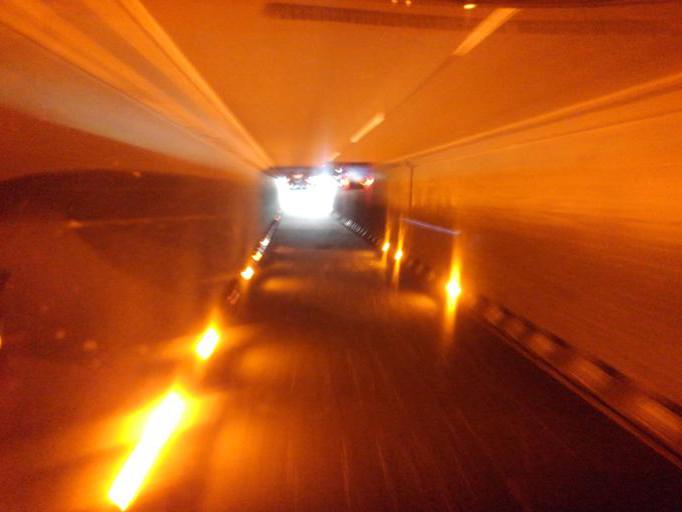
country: JP
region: Saitama
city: Sayama
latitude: 35.8233
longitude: 139.3798
